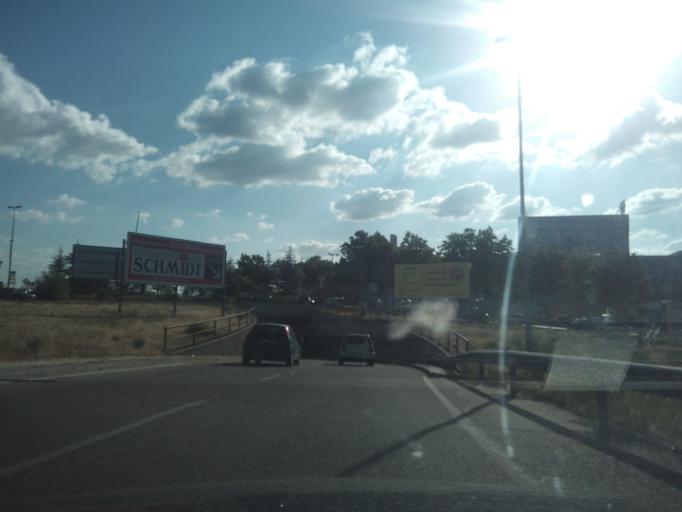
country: ES
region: Madrid
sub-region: Provincia de Madrid
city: San Sebastian de los Reyes
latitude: 40.5476
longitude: -3.6093
